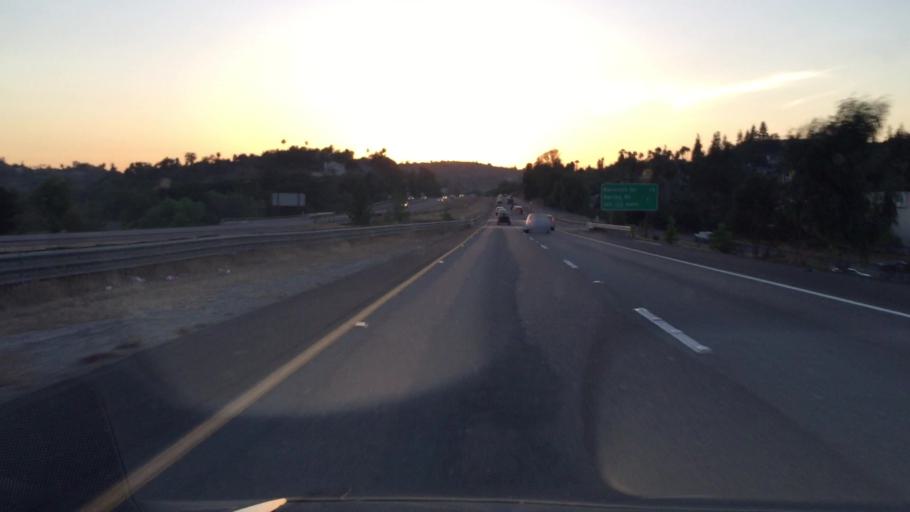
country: US
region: California
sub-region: San Diego County
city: Spring Valley
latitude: 32.7462
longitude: -116.9887
